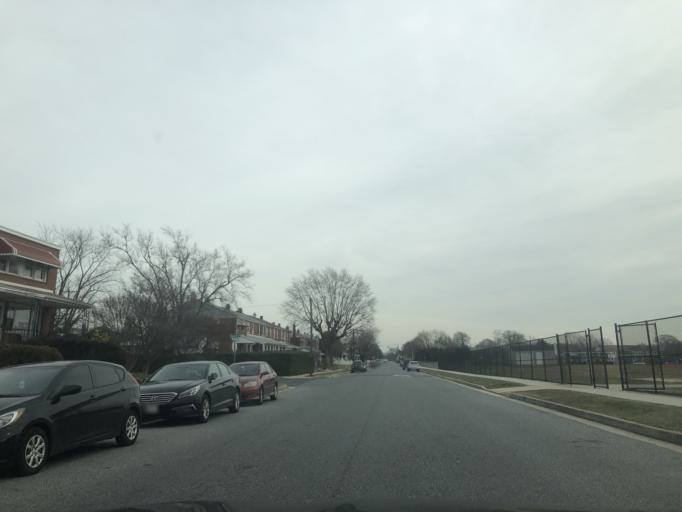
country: US
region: Maryland
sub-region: Baltimore County
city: Dundalk
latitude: 39.2681
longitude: -76.4881
